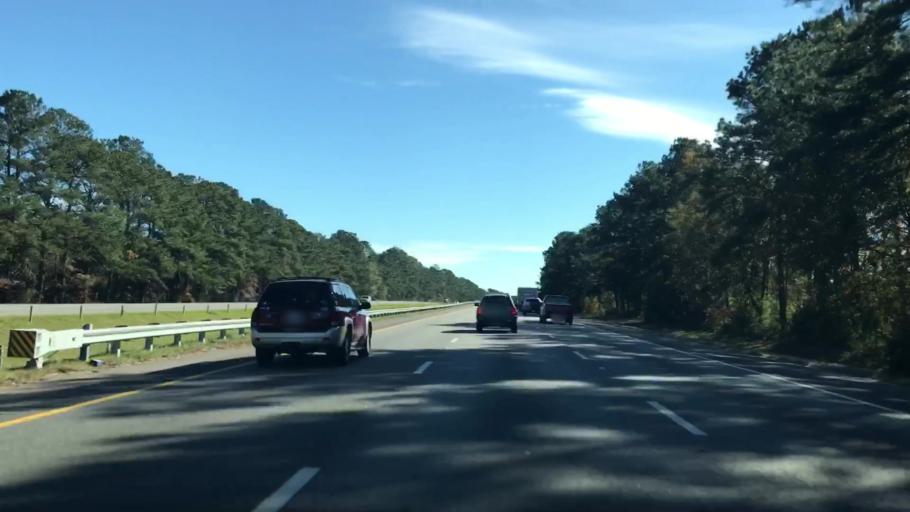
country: US
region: South Carolina
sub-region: Berkeley County
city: Ladson
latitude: 33.0066
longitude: -80.1049
